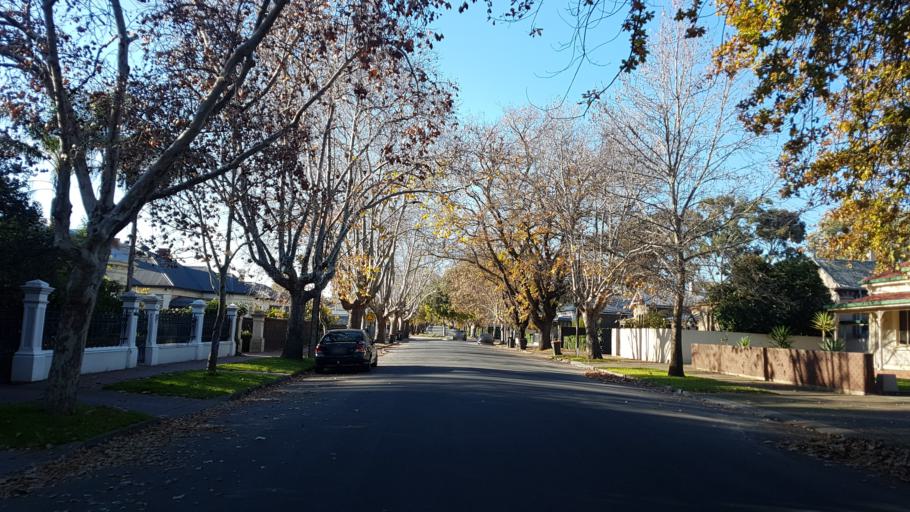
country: AU
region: South Australia
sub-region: Norwood Payneham St Peters
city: Royston Park
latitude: -34.9100
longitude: 138.6226
